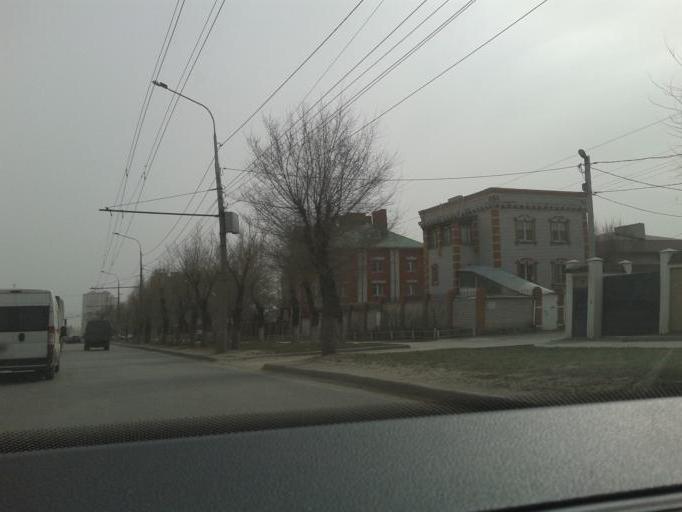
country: RU
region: Volgograd
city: Volgograd
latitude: 48.7313
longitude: 44.4969
